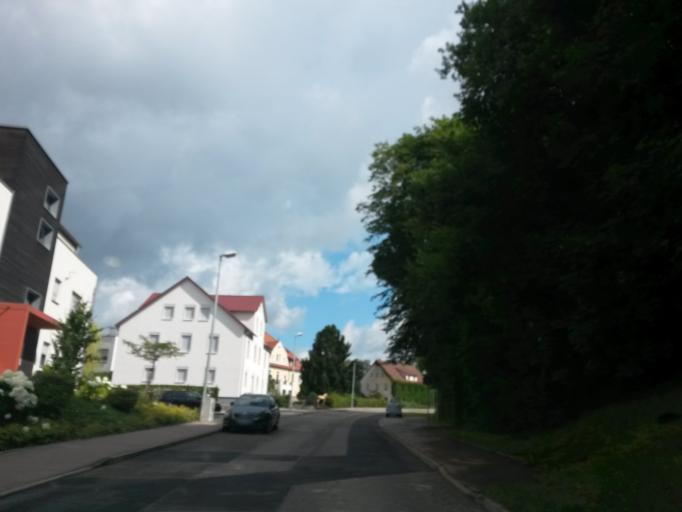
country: DE
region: Baden-Wuerttemberg
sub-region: Regierungsbezirk Stuttgart
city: Ellwangen
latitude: 48.9636
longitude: 10.1348
